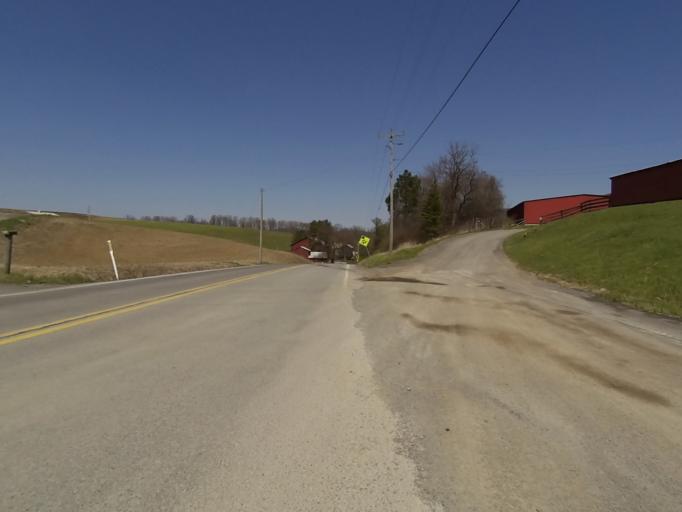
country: US
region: Pennsylvania
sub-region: Blair County
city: Tyrone
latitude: 40.5978
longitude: -78.1346
